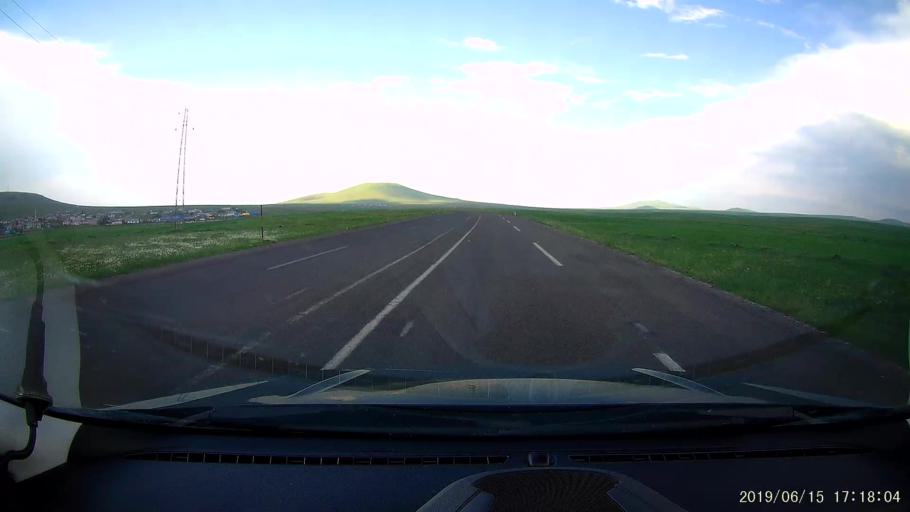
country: TR
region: Kars
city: Kars
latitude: 40.6138
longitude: 43.2507
